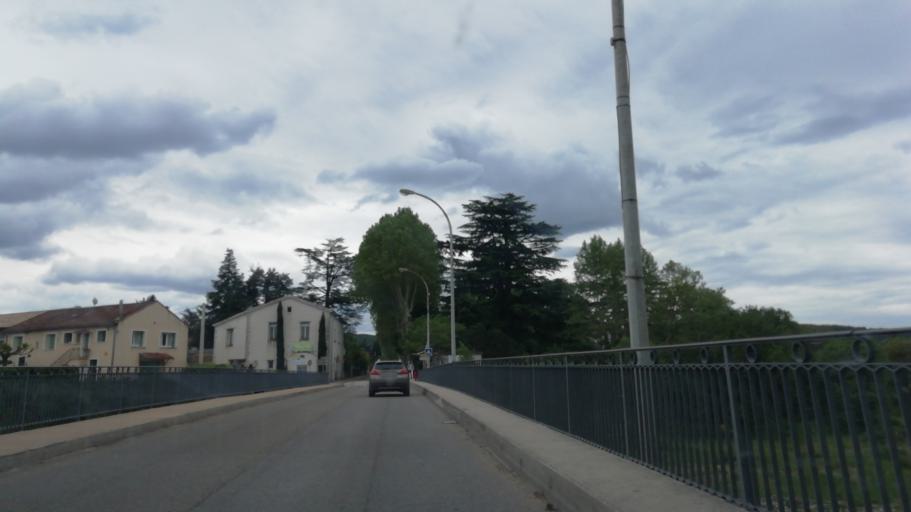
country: FR
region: Languedoc-Roussillon
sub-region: Departement de l'Herault
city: Ganges
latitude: 43.9317
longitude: 3.7114
